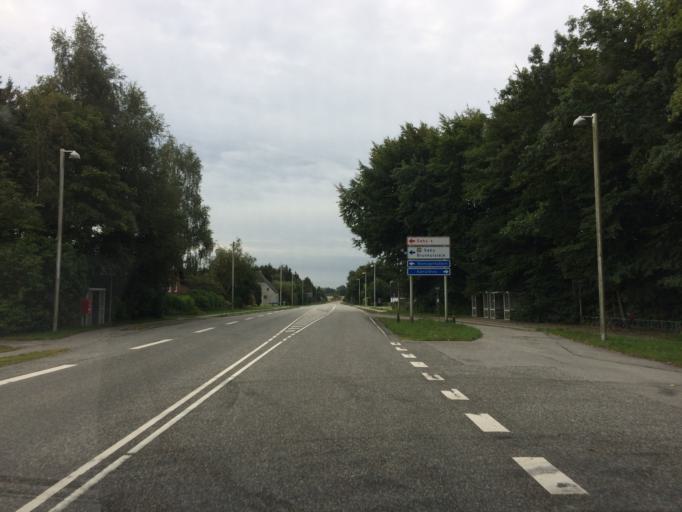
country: DK
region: Central Jutland
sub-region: Herning Kommune
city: Lind
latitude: 56.0652
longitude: 8.9917
